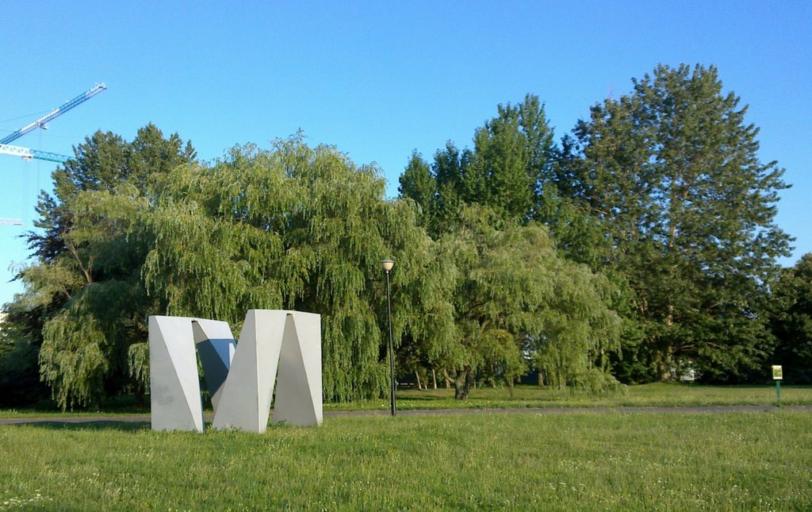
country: PL
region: Pomeranian Voivodeship
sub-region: Sopot
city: Sopot
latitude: 54.3975
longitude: 18.5980
